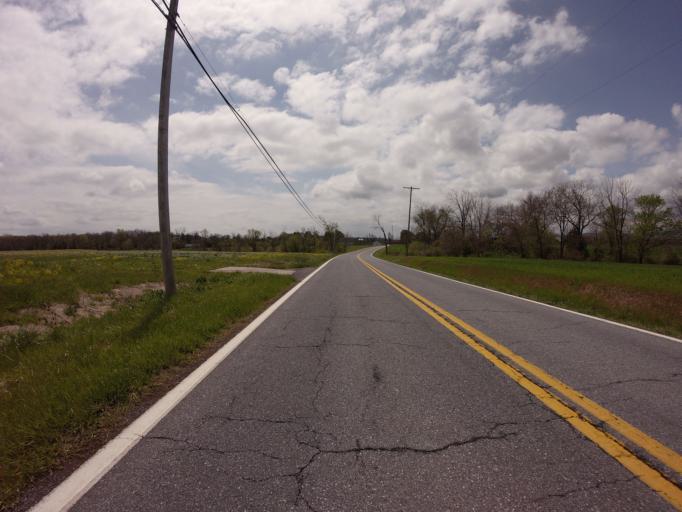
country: US
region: Maryland
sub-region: Frederick County
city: Emmitsburg
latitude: 39.6723
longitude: -77.3356
